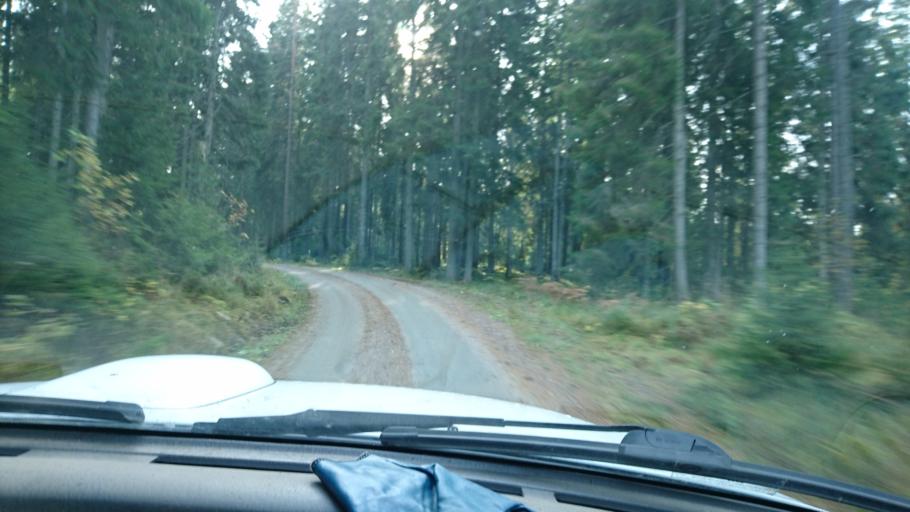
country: SE
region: Vaestra Goetaland
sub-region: Ulricehamns Kommun
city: Ulricehamn
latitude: 57.9443
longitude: 13.5412
